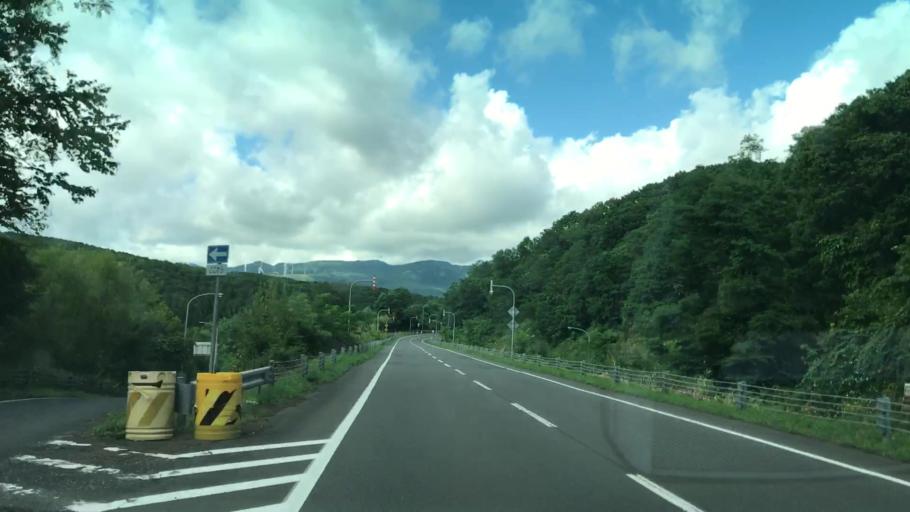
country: JP
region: Hokkaido
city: Muroran
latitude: 42.3730
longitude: 140.9614
